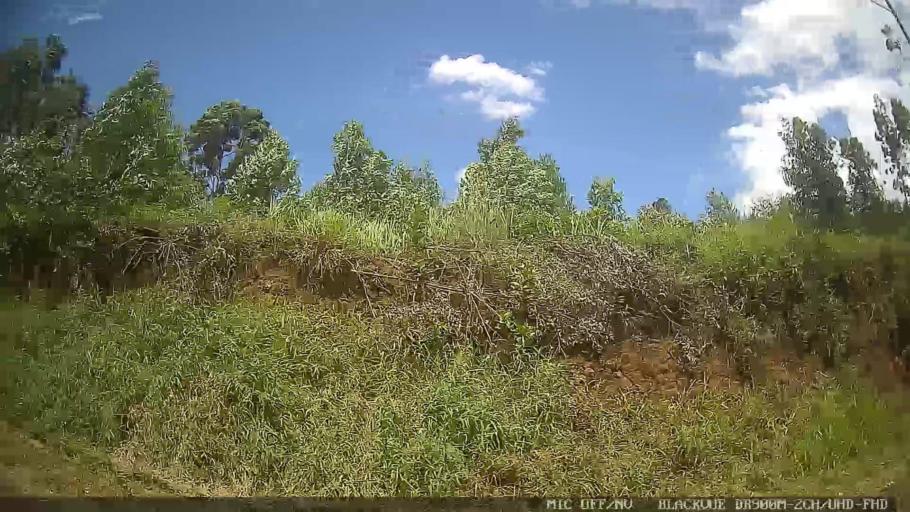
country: BR
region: Minas Gerais
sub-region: Extrema
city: Extrema
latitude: -22.7488
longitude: -46.4327
